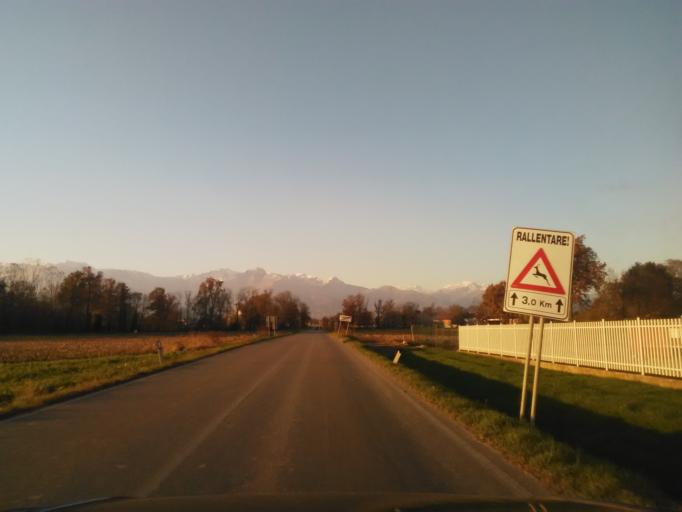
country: IT
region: Piedmont
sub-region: Provincia di Biella
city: Cerrione
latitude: 45.4830
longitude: 8.0719
